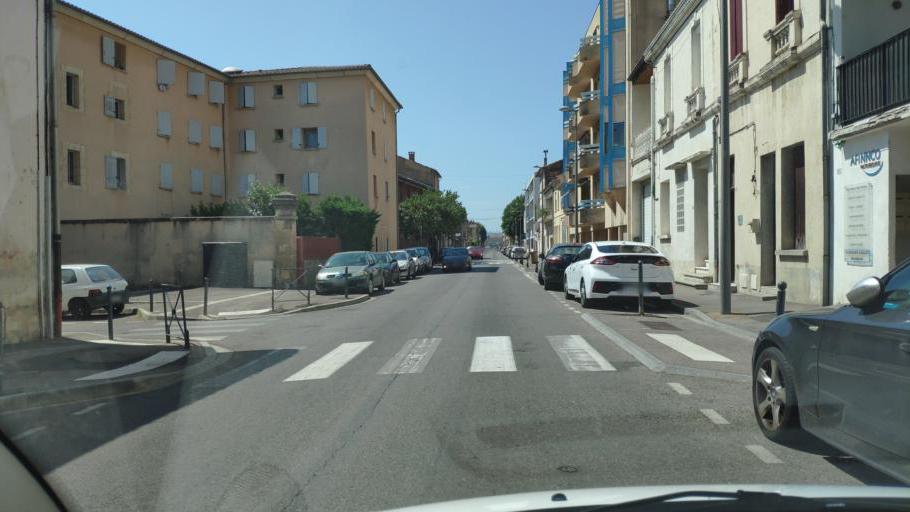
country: FR
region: Provence-Alpes-Cote d'Azur
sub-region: Departement du Vaucluse
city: Cavaillon
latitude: 43.8388
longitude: 5.0361
